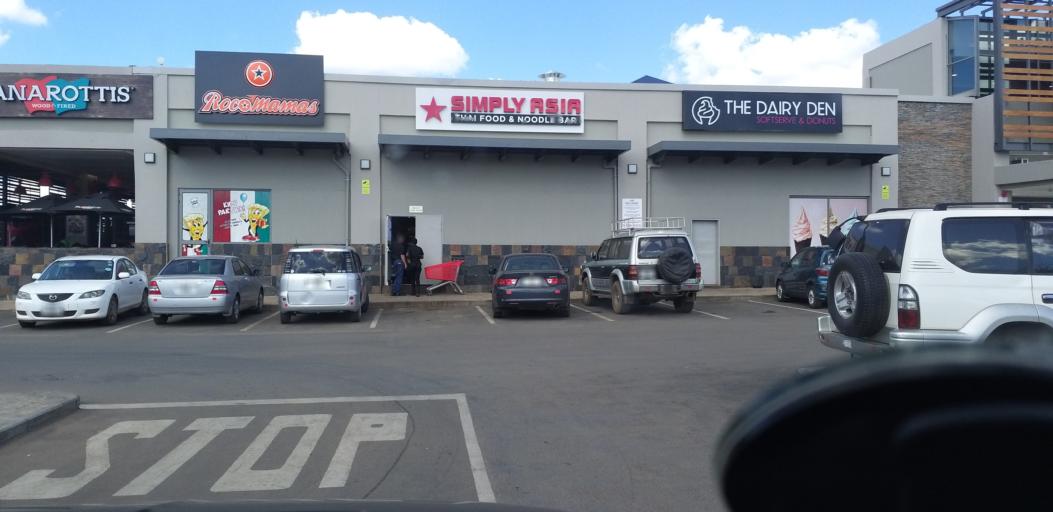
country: ZM
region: Lusaka
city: Lusaka
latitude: -15.4318
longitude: 28.3417
